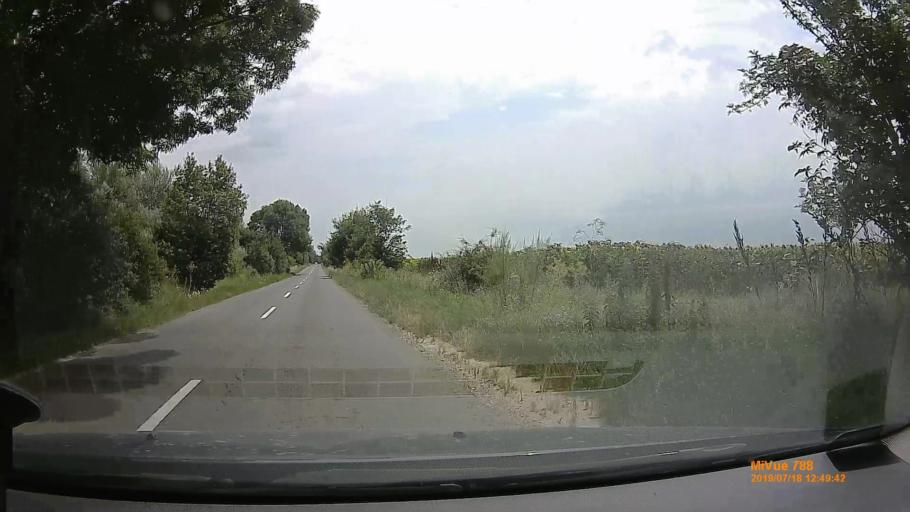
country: HU
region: Pest
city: Perbal
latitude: 47.5740
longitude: 18.7821
